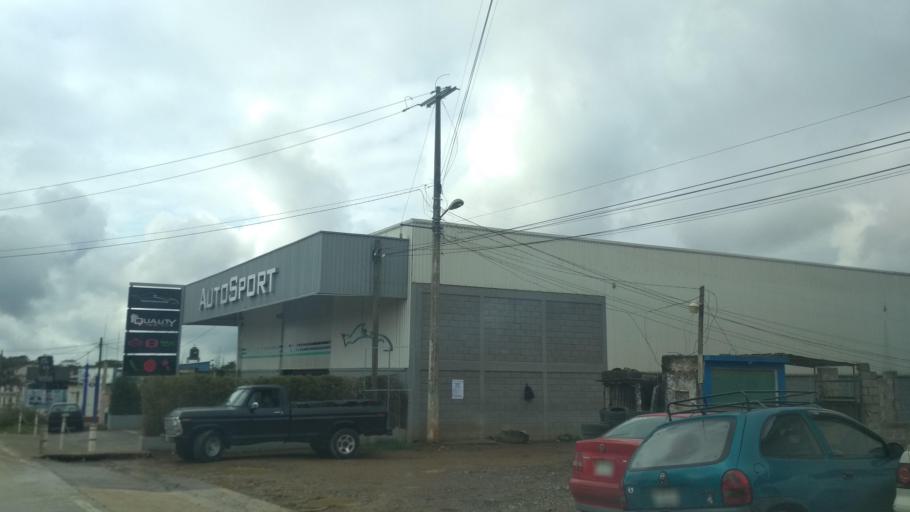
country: MX
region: Veracruz
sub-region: Emiliano Zapata
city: Jacarandas
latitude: 19.4970
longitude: -96.8603
